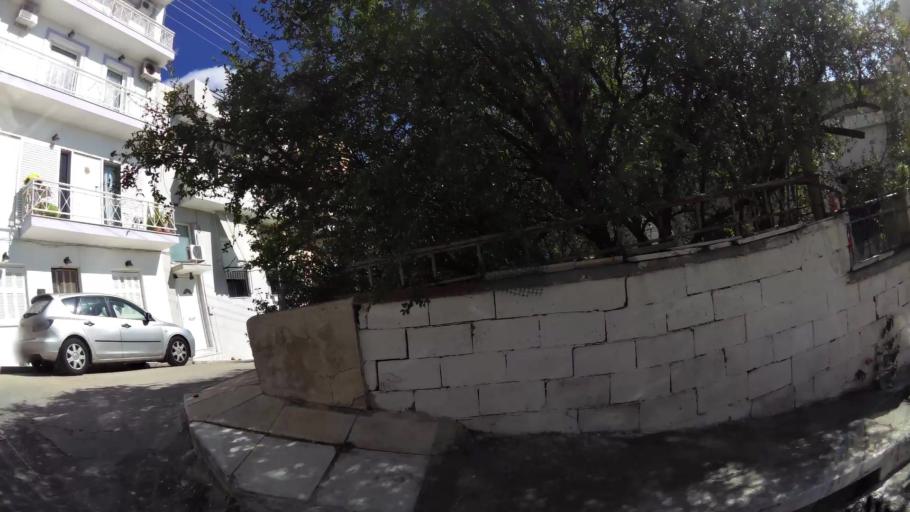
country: GR
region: Attica
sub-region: Nomos Piraios
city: Perama
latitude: 37.9643
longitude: 23.5766
